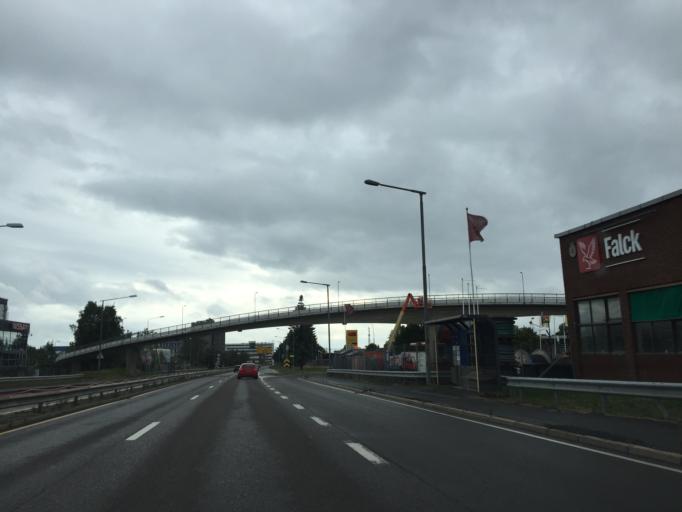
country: NO
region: Oslo
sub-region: Oslo
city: Oslo
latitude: 59.9316
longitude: 10.8248
